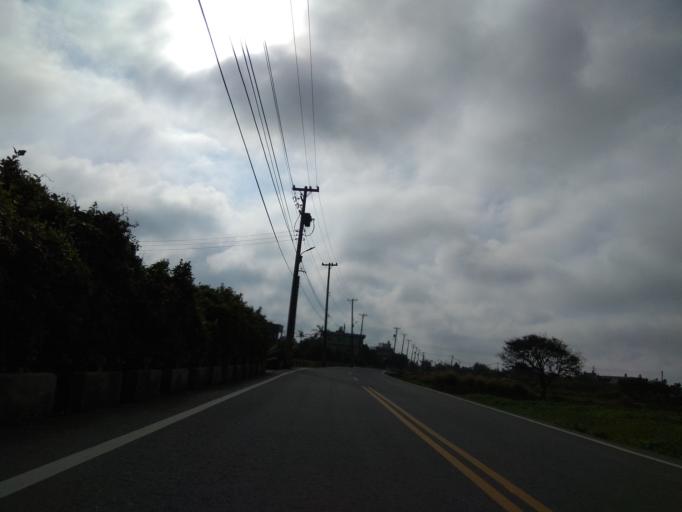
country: TW
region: Taiwan
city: Taoyuan City
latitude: 25.0678
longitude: 121.1583
